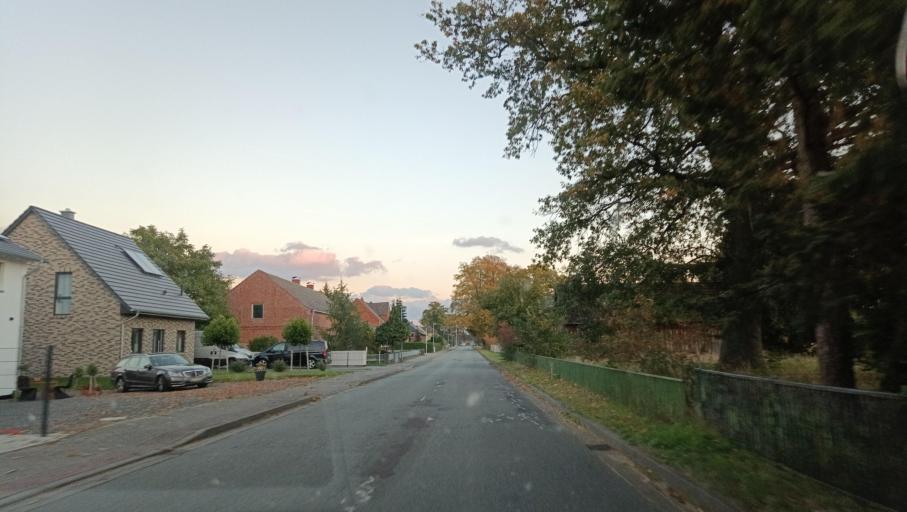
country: DE
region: Mecklenburg-Vorpommern
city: Ludwigslust
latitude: 53.2797
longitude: 11.4922
